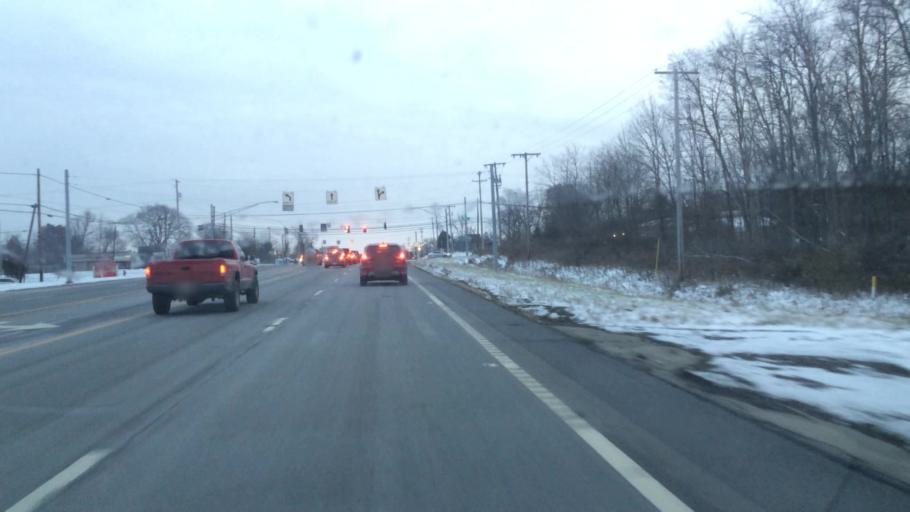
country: US
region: Ohio
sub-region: Summit County
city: Montrose-Ghent
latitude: 41.1361
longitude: -81.7369
